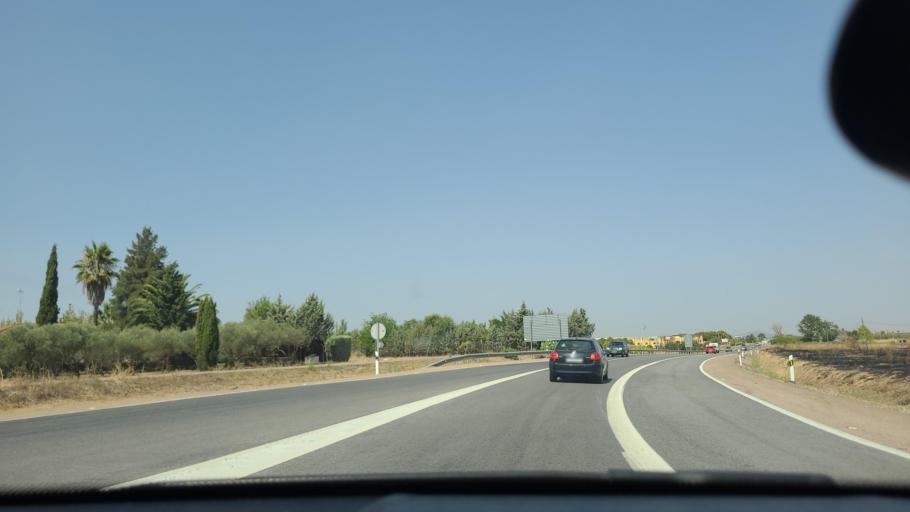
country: ES
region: Extremadura
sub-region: Provincia de Badajoz
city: Puebla de Sancho Perez
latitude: 38.3984
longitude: -6.3486
